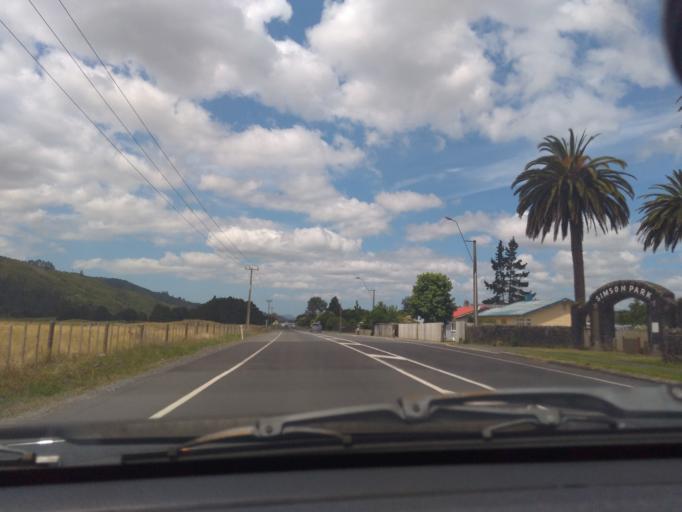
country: NZ
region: Northland
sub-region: Far North District
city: Moerewa
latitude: -35.3870
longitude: 174.0165
